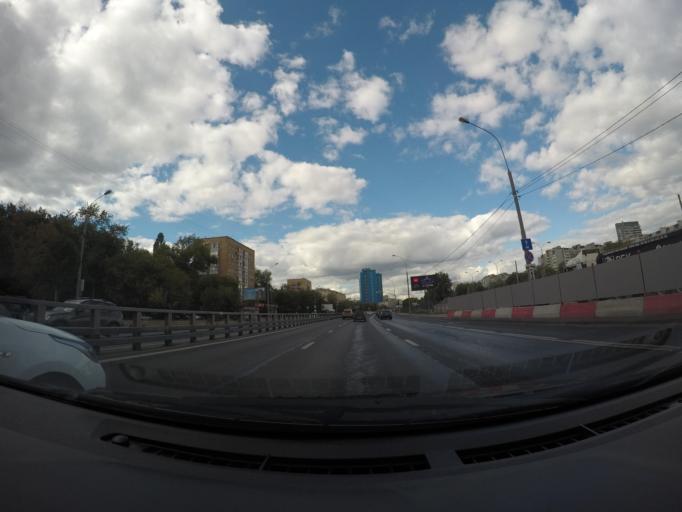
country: RU
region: Moscow
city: Likhobory
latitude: 55.8210
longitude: 37.5736
